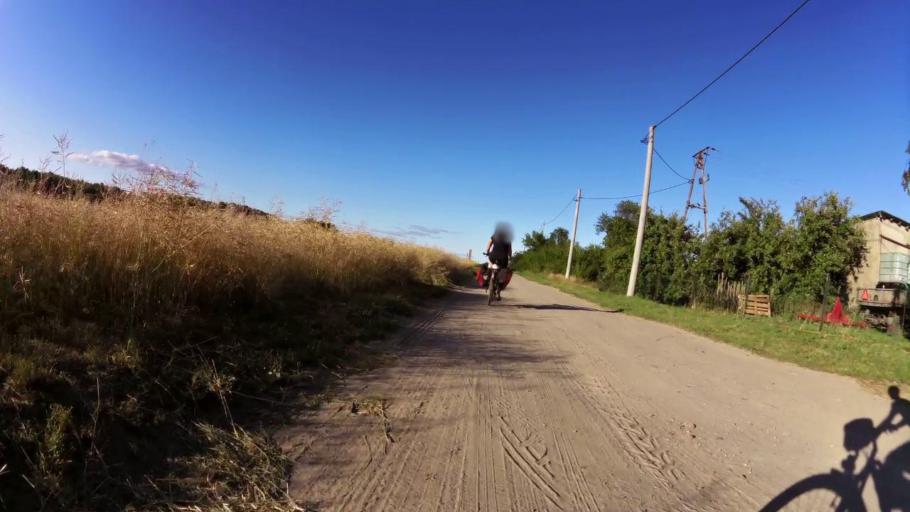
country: PL
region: West Pomeranian Voivodeship
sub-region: Powiat swidwinski
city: Swidwin
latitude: 53.7341
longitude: 15.8538
